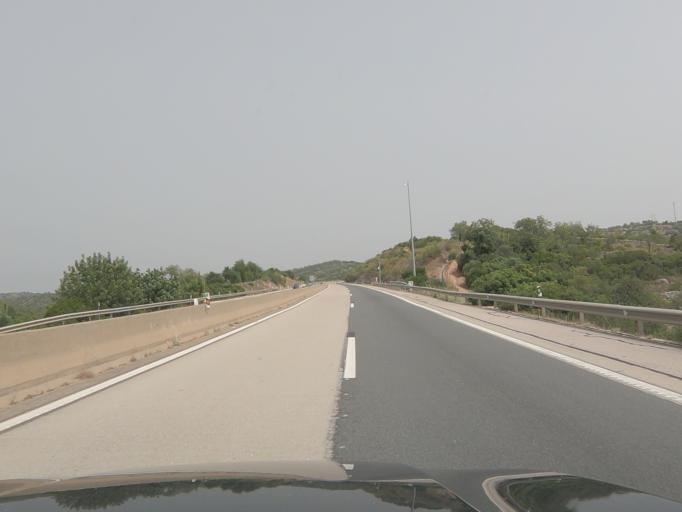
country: PT
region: Faro
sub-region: Loule
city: Boliqueime
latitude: 37.1609
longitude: -8.1893
